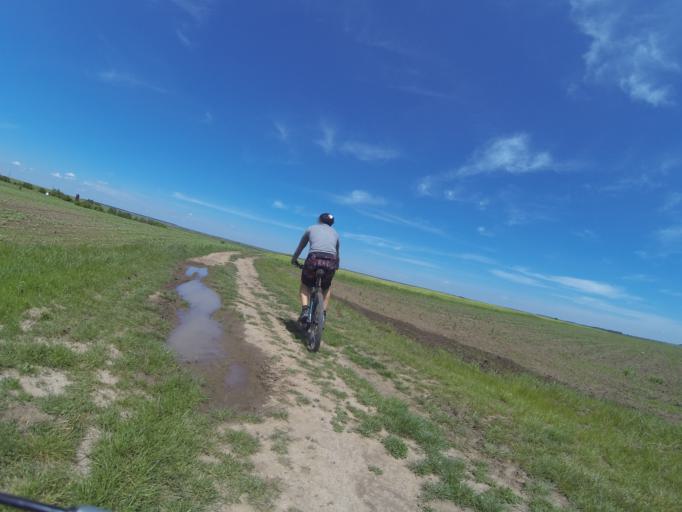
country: RO
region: Dolj
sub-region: Comuna Teslui
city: Teslui
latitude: 44.1971
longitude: 24.1408
